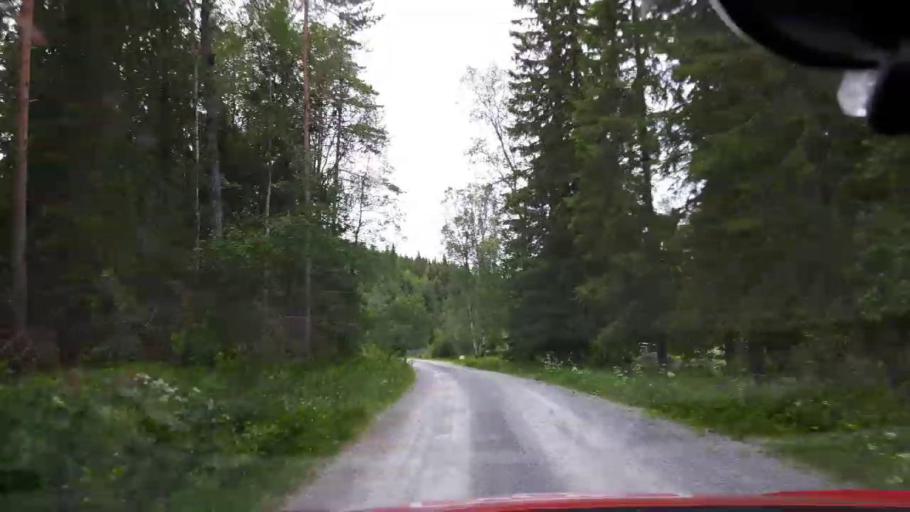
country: SE
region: Jaemtland
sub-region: OEstersunds Kommun
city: Brunflo
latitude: 63.0345
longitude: 14.9285
